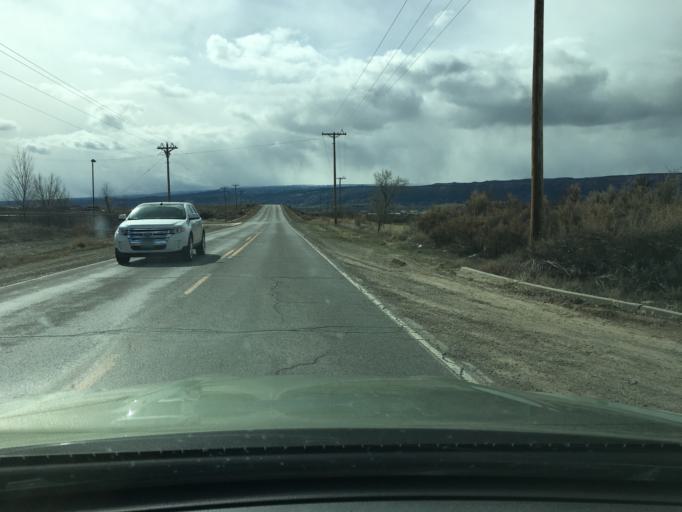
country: US
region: Colorado
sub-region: Mesa County
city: Redlands
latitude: 39.1170
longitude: -108.6267
